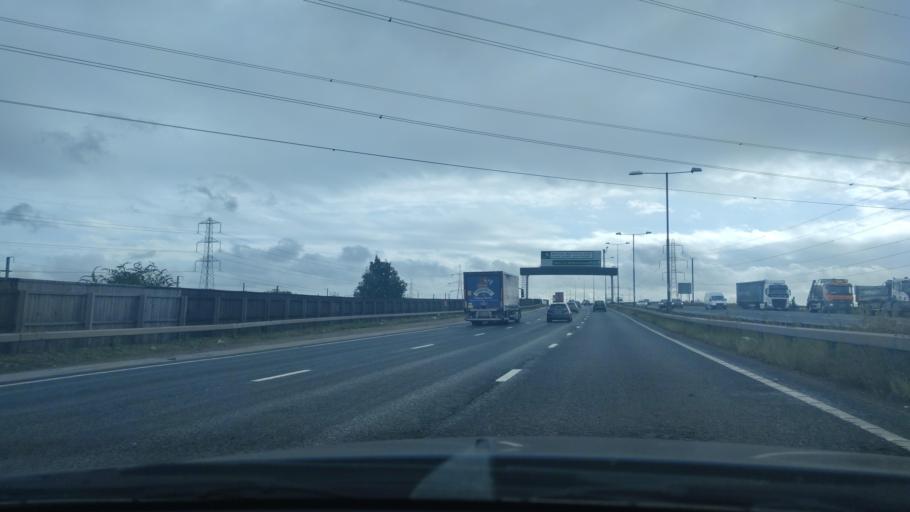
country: GB
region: England
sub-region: Essex
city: Purfleet
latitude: 51.5041
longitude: 0.2094
